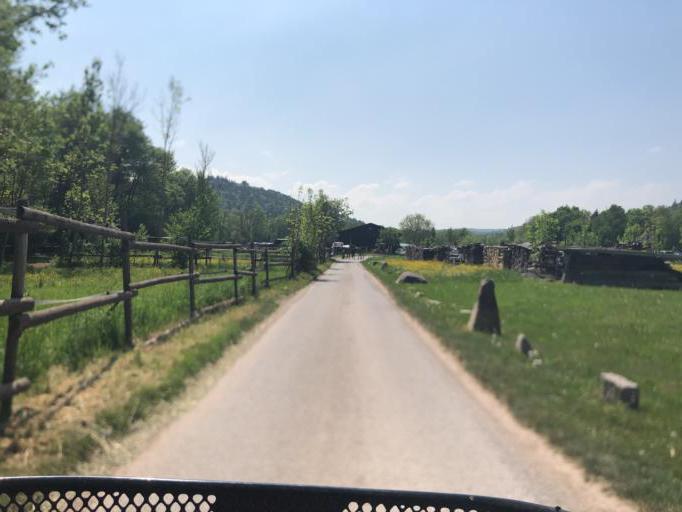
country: DE
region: Baden-Wuerttemberg
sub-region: Tuebingen Region
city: Rottenburg
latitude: 48.4794
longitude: 8.9974
